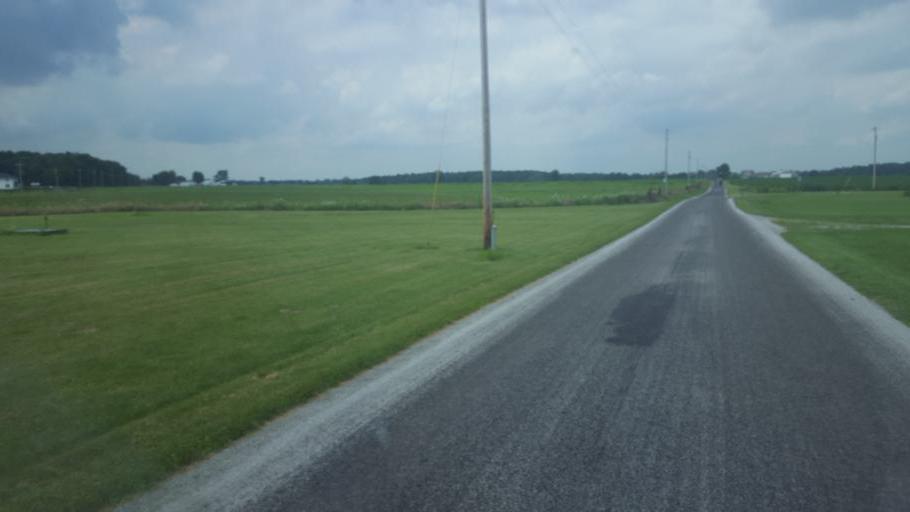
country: US
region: Ohio
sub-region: Hardin County
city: Kenton
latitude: 40.5836
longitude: -83.5190
